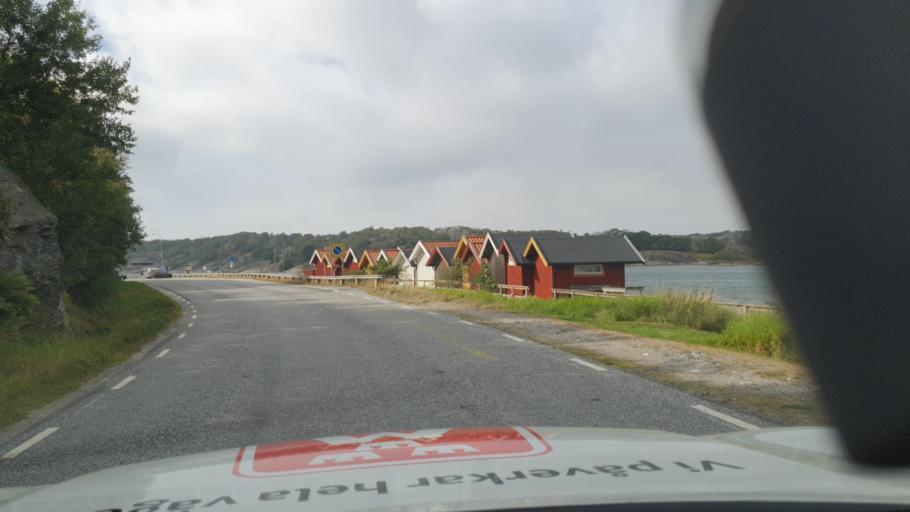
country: SE
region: Vaestra Goetaland
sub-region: Lysekils Kommun
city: Lysekil
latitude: 58.1956
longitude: 11.4920
